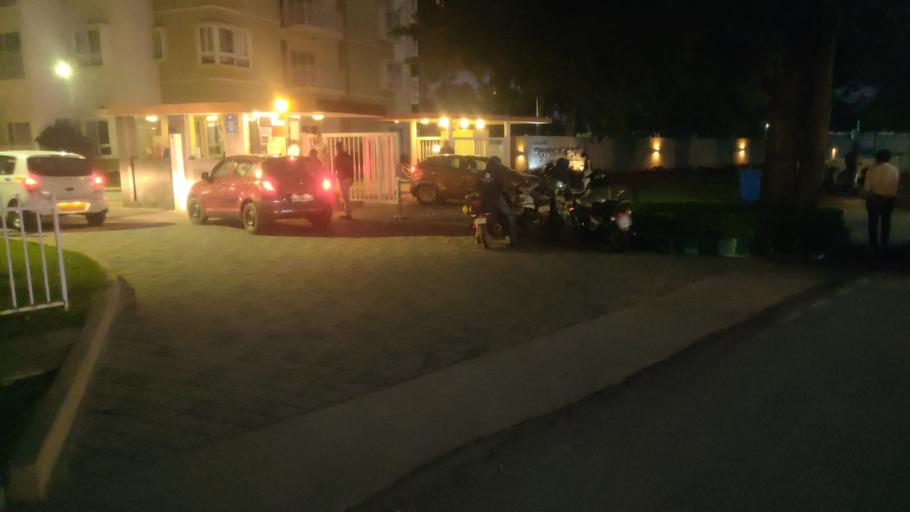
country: IN
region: Karnataka
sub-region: Bangalore Urban
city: Yelahanka
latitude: 13.0936
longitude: 77.5943
